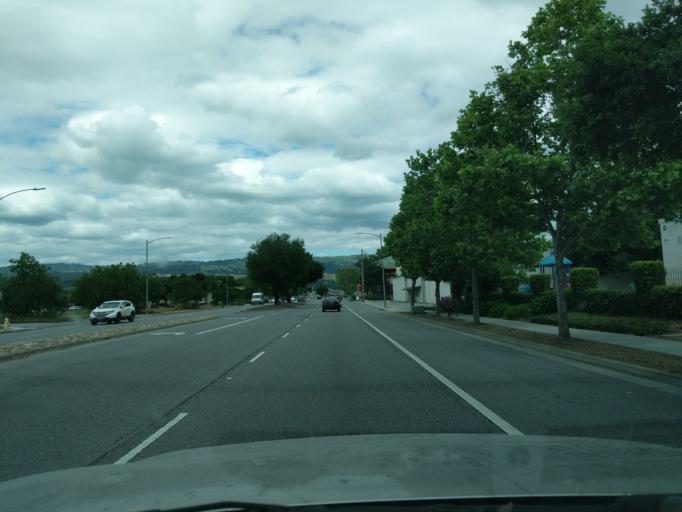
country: US
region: California
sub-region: Santa Clara County
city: Morgan Hill
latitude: 37.1289
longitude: -121.6405
